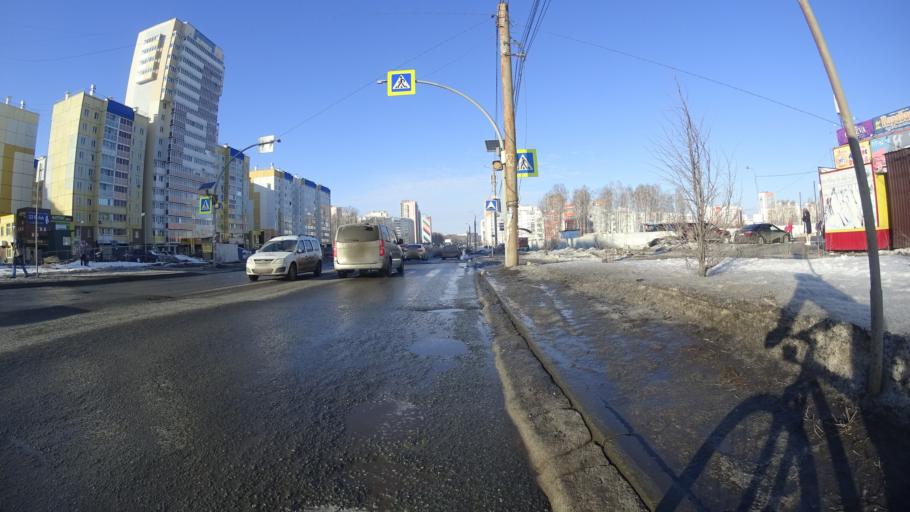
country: RU
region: Chelyabinsk
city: Roshchino
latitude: 55.2037
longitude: 61.2844
